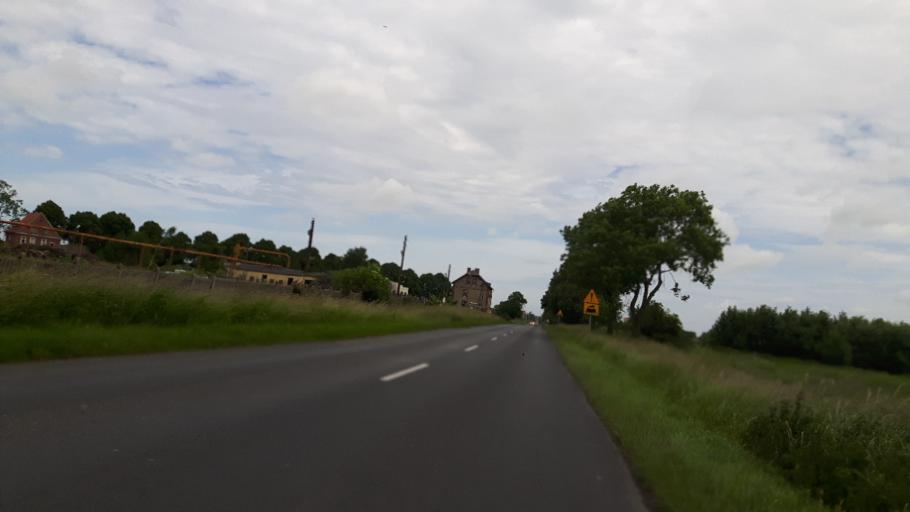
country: PL
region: West Pomeranian Voivodeship
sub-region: Powiat gryficki
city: Trzebiatow
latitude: 54.0451
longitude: 15.2515
